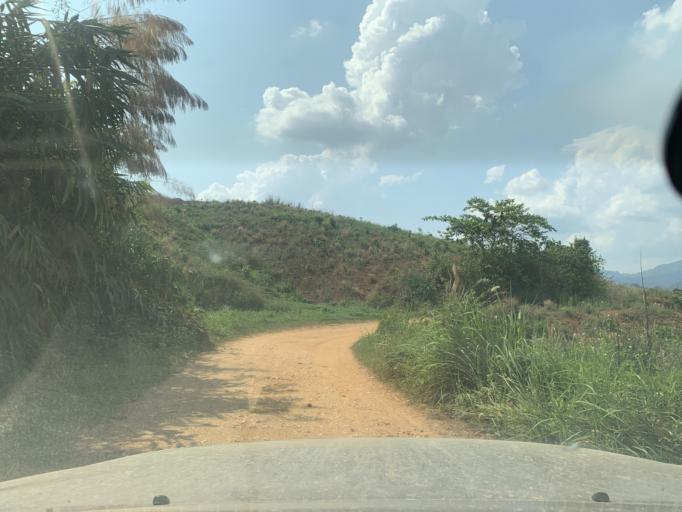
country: TH
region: Phayao
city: Phu Sang
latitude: 19.7028
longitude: 100.4912
